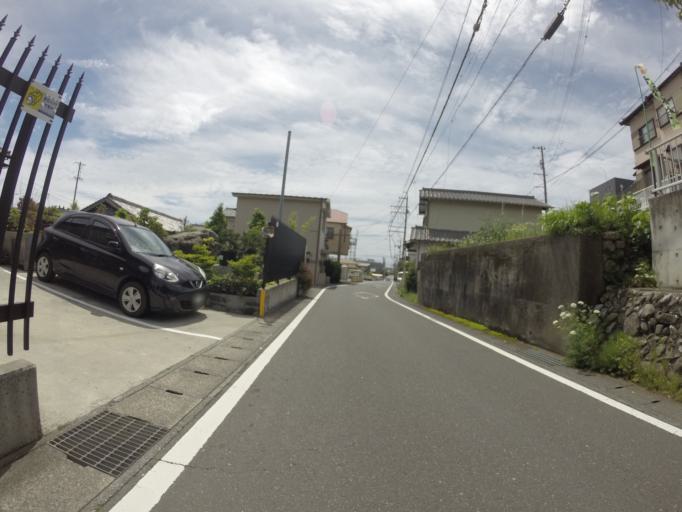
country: JP
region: Shizuoka
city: Fujinomiya
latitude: 35.1100
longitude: 138.5601
